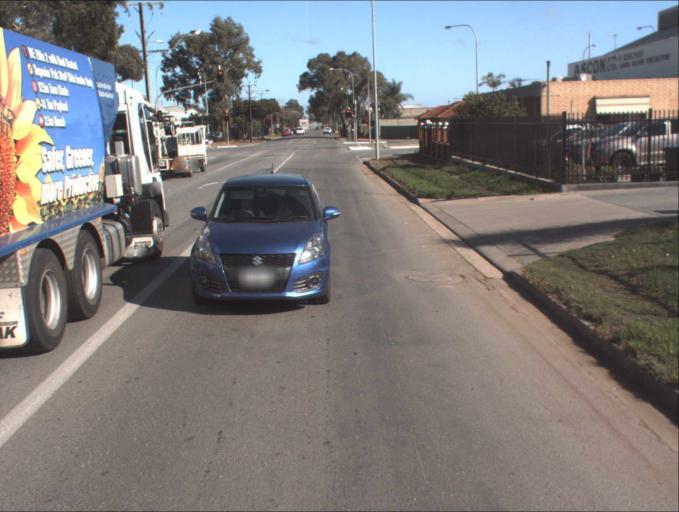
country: AU
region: South Australia
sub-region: Charles Sturt
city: Woodville North
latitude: -34.8413
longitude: 138.5470
